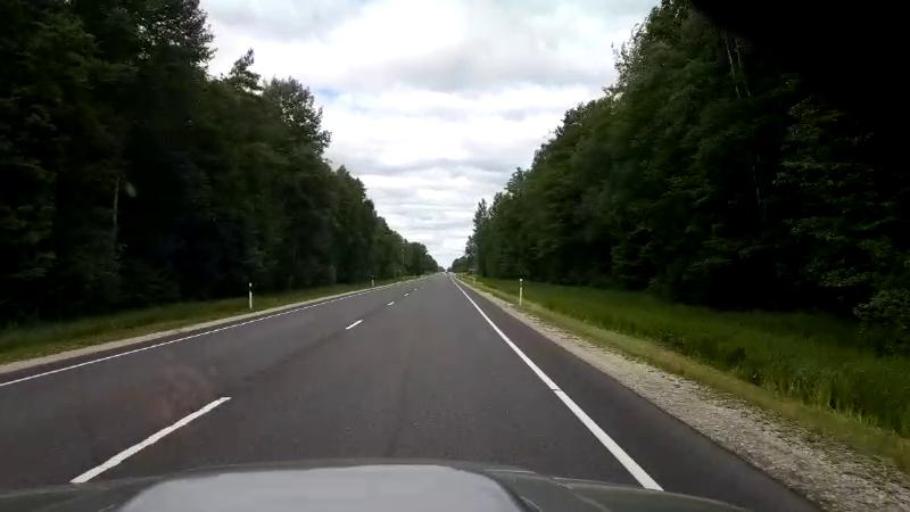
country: EE
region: Raplamaa
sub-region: Maerjamaa vald
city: Marjamaa
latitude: 58.8306
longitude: 24.4181
